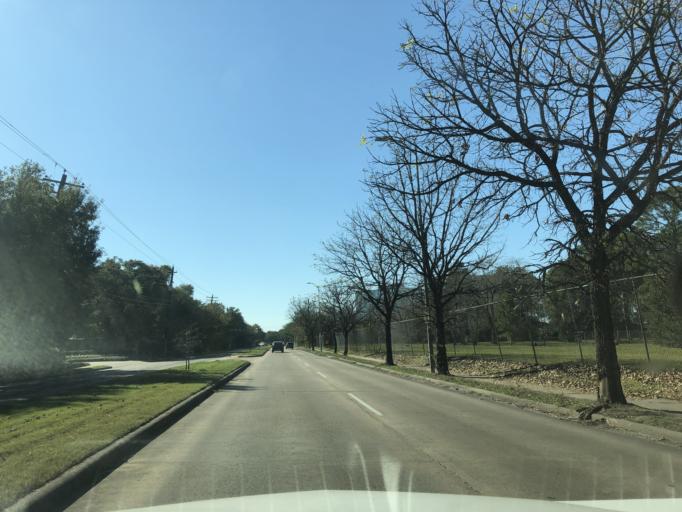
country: US
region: Texas
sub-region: Fort Bend County
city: Missouri City
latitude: 29.6796
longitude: -95.5231
